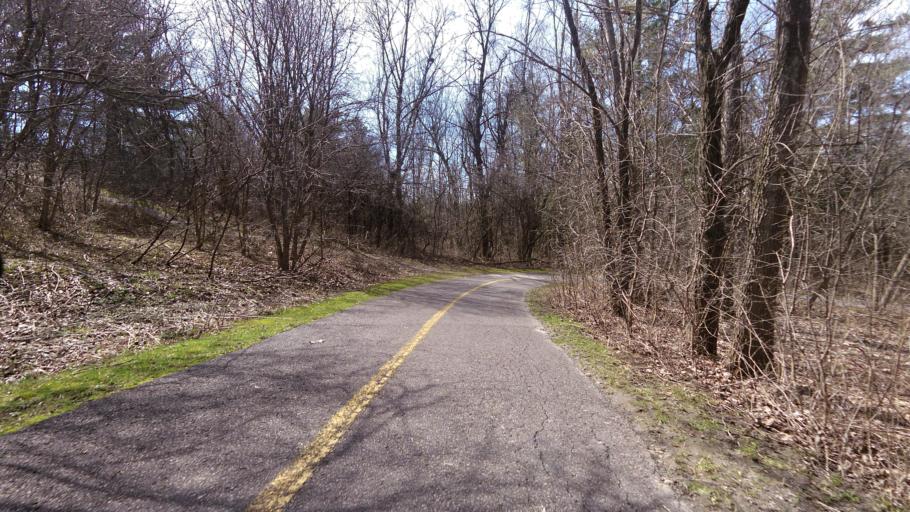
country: CA
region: Ontario
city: Ottawa
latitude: 45.4411
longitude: -75.7534
